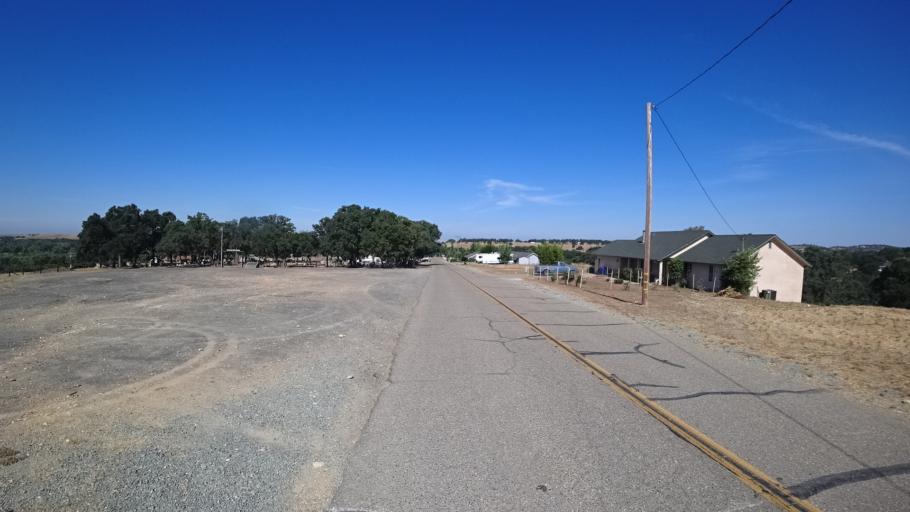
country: US
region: California
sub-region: Calaveras County
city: Rancho Calaveras
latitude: 38.0991
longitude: -120.8705
